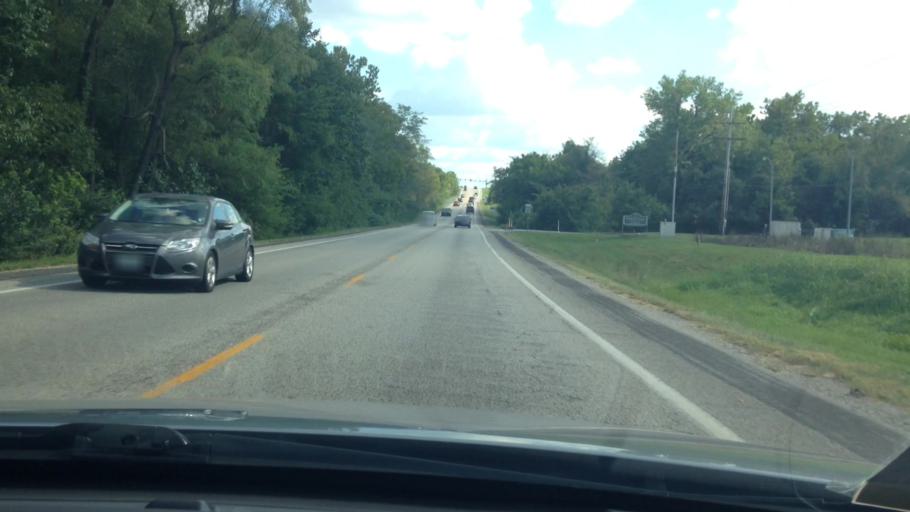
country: US
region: Missouri
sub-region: Clay County
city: Liberty
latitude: 39.2852
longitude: -94.4696
